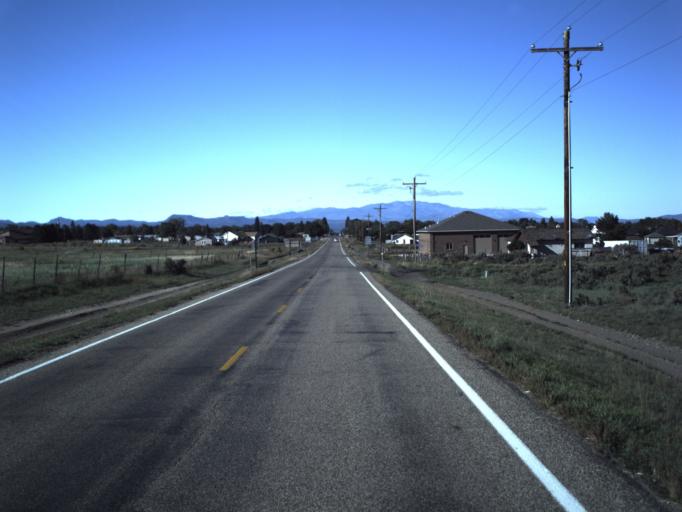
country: US
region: Utah
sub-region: Garfield County
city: Panguitch
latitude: 37.8084
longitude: -112.4354
